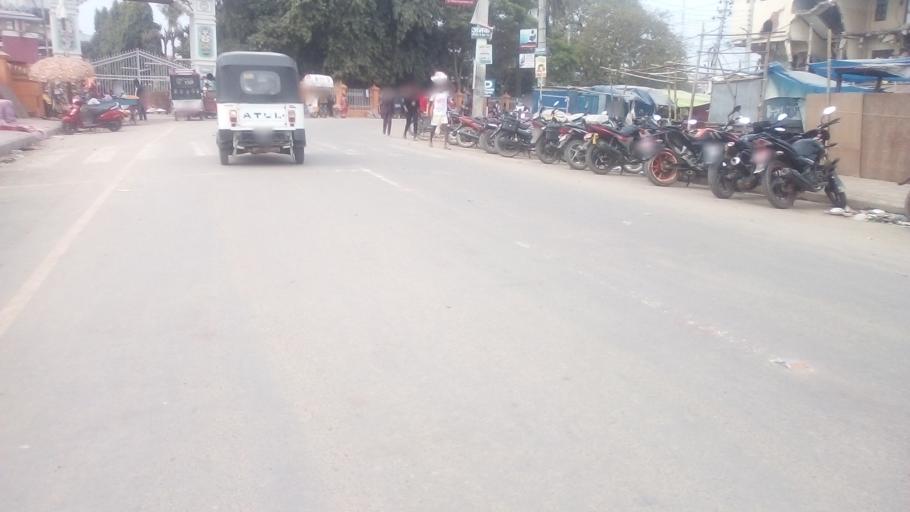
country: NP
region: Central Region
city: Janakpur
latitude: 26.7309
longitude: 85.9263
